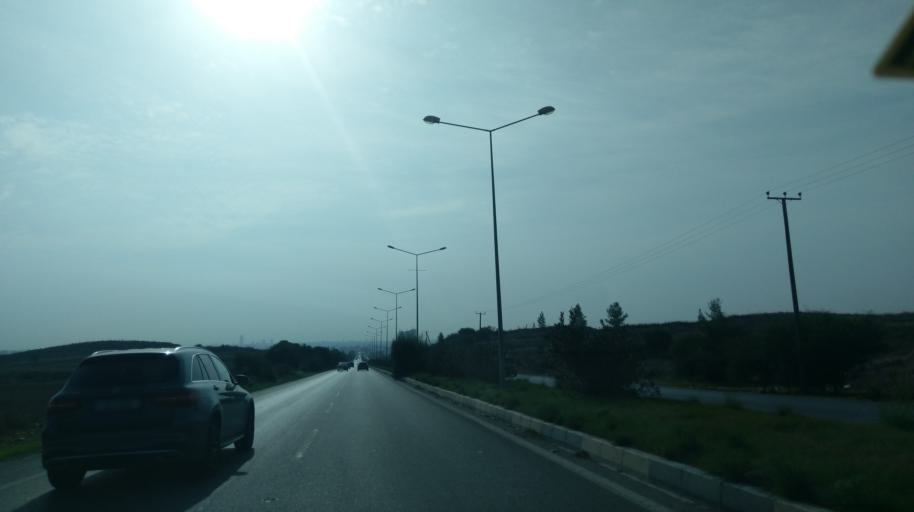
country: CY
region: Lefkosia
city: Nicosia
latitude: 35.2262
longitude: 33.3139
